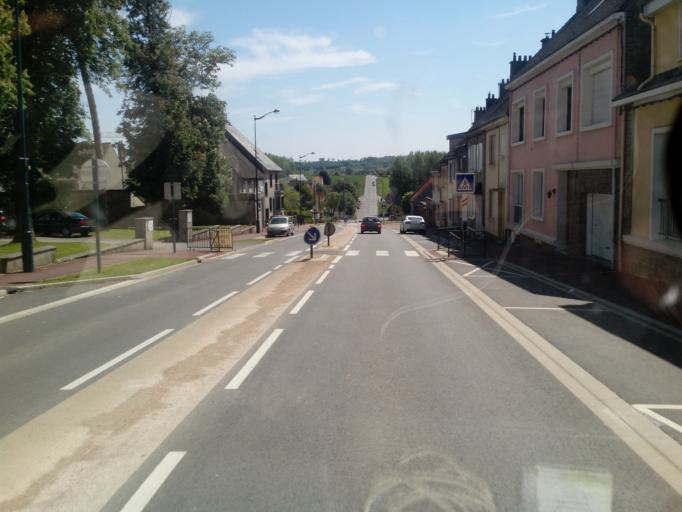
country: FR
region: Nord-Pas-de-Calais
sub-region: Departement du Pas-de-Calais
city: Samer
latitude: 50.6370
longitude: 1.7430
